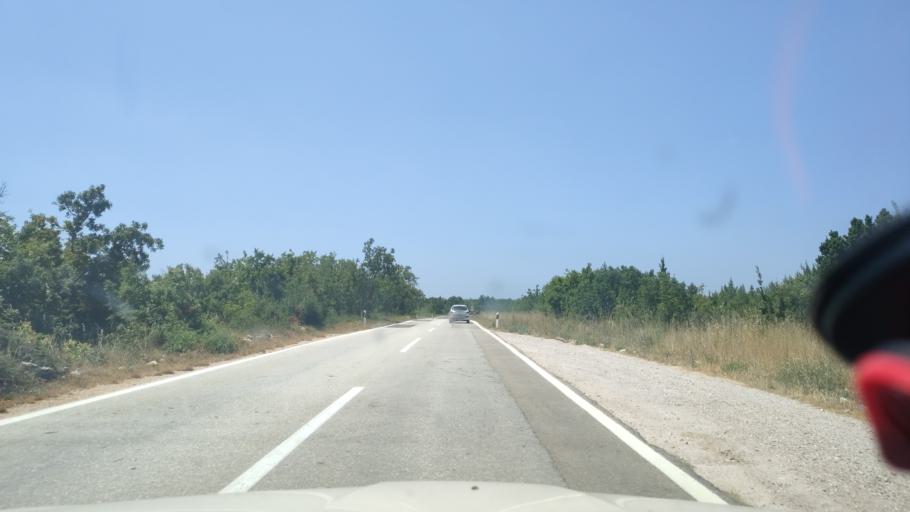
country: HR
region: Sibensko-Kniniska
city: Kistanje
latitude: 43.9715
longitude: 15.9090
